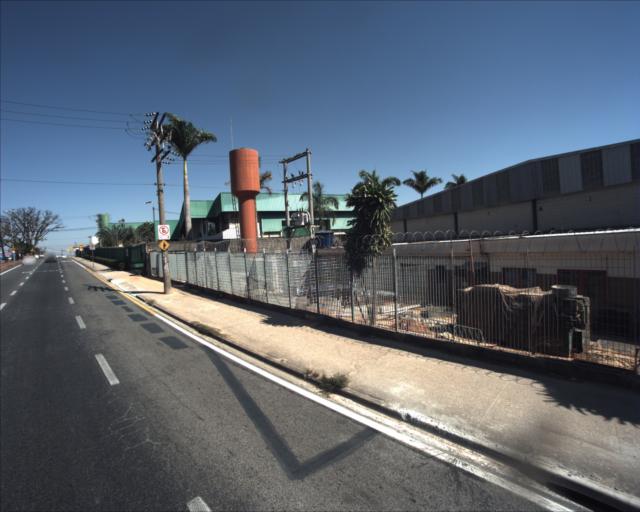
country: BR
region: Sao Paulo
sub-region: Sorocaba
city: Sorocaba
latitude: -23.4486
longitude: -47.4800
